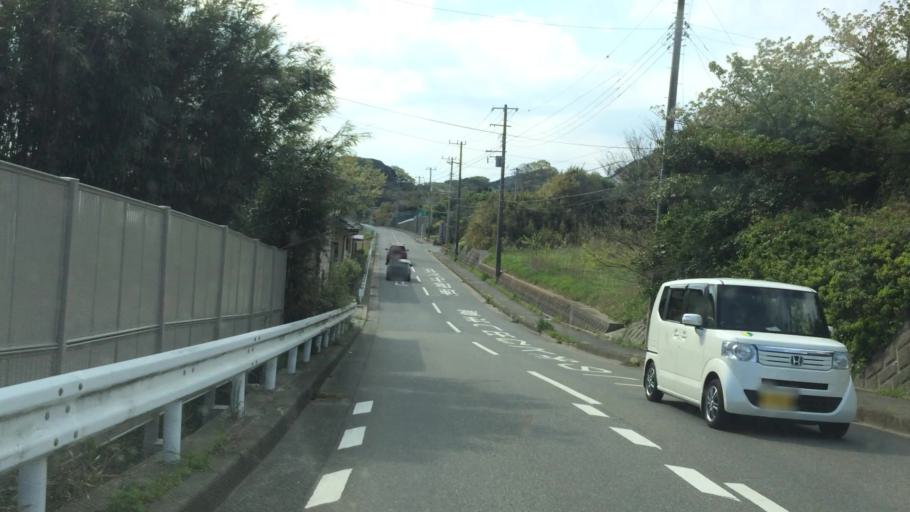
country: JP
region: Kanagawa
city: Yokosuka
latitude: 35.2326
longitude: 139.6292
